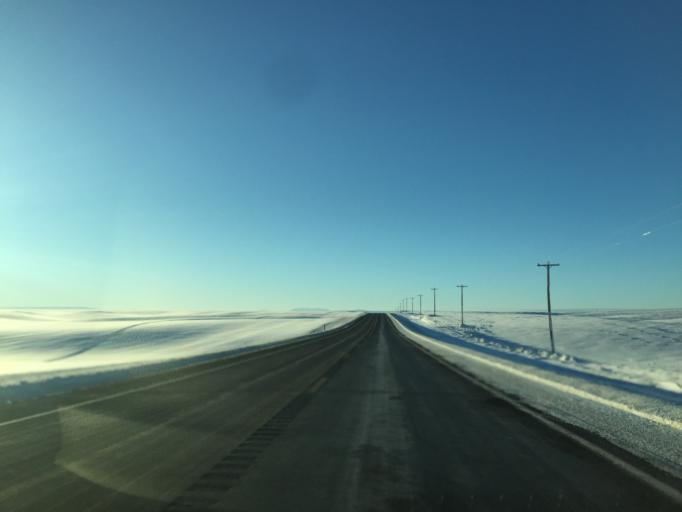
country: US
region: Washington
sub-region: Grant County
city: Soap Lake
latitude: 47.5994
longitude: -119.5638
